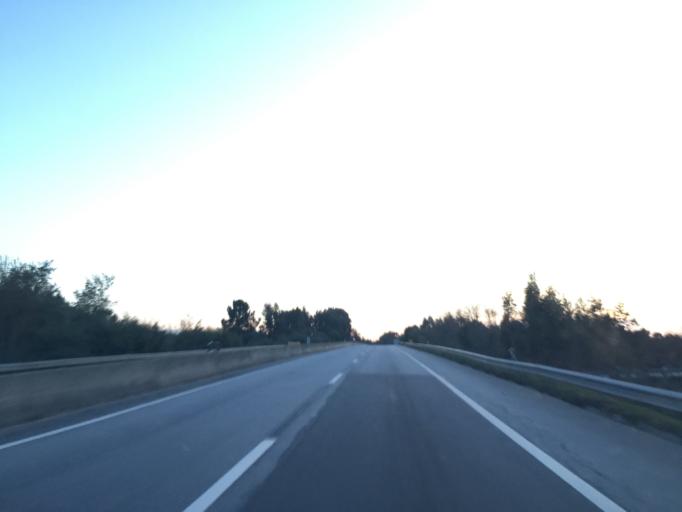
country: PT
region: Viseu
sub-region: Concelho de Carregal do Sal
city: Carregal do Sal
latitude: 40.4266
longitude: -8.0242
